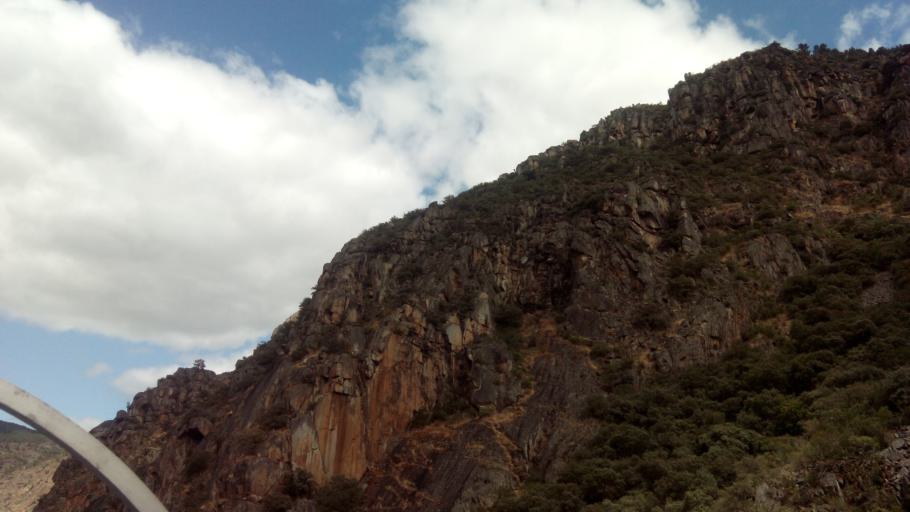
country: ES
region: Galicia
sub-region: Provincia de Lugo
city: Lobios
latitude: 42.3927
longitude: -7.5566
